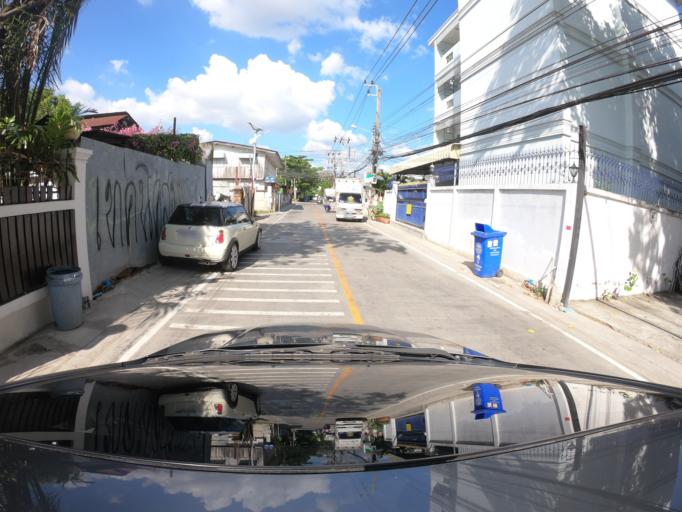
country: TH
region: Bangkok
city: Bang Na
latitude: 13.6488
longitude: 100.6247
